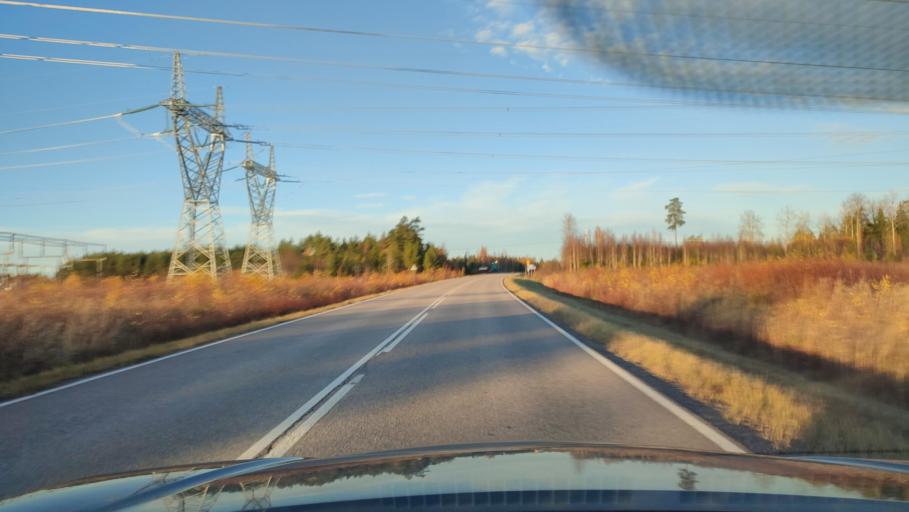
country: FI
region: Ostrobothnia
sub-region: Sydosterbotten
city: Kristinestad
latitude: 62.2916
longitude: 21.3794
